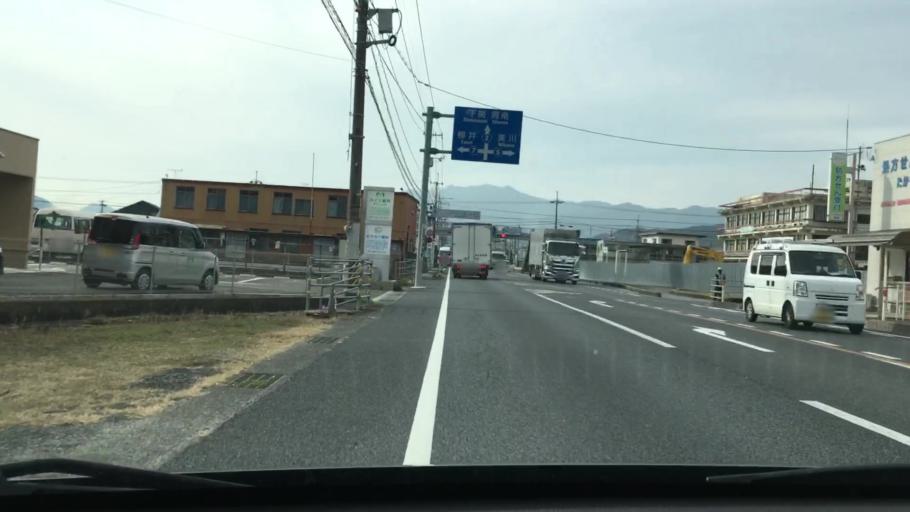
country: JP
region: Yamaguchi
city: Yanai
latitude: 34.0928
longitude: 132.0525
